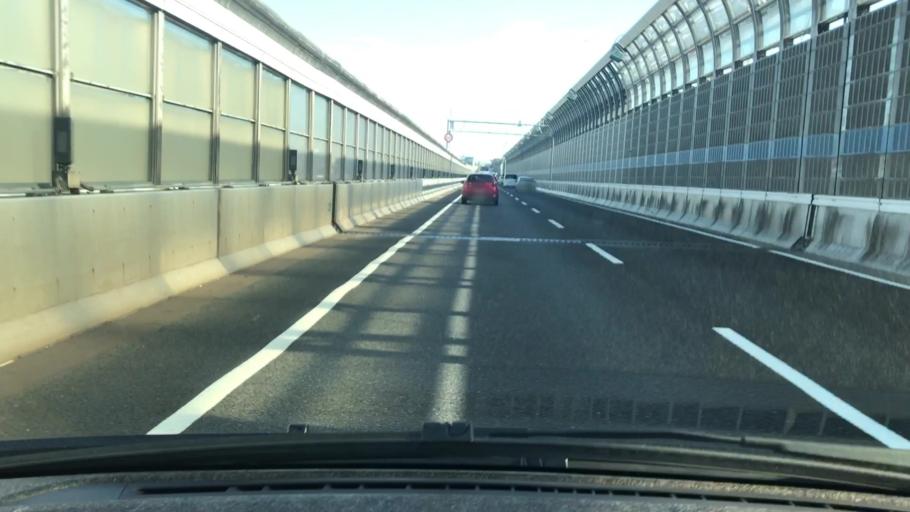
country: JP
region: Hyogo
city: Ashiya
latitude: 34.7217
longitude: 135.2932
